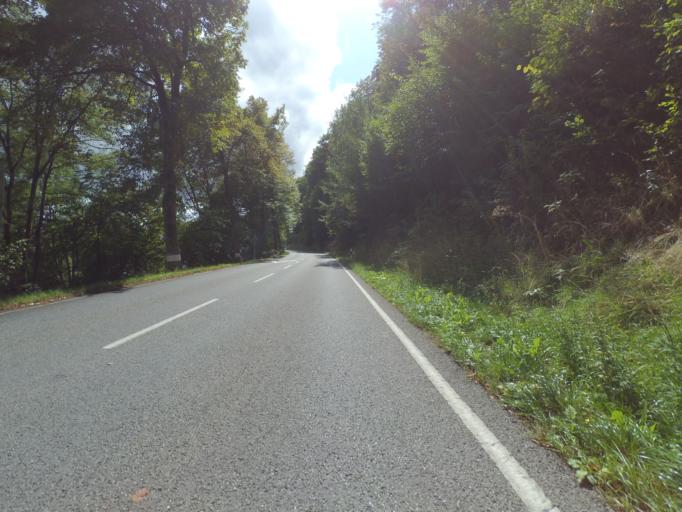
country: LU
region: Grevenmacher
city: Gonderange
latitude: 49.6628
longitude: 6.2279
